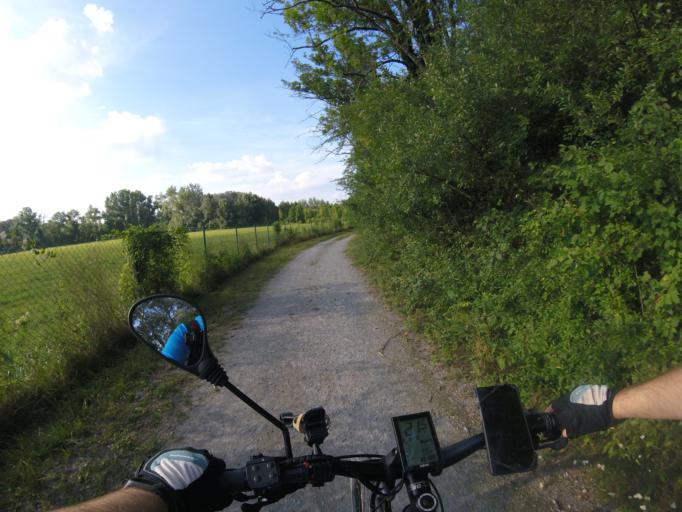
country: AT
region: Lower Austria
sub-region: Politischer Bezirk Baden
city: Ebreichsdorf
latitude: 47.9722
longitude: 16.3885
